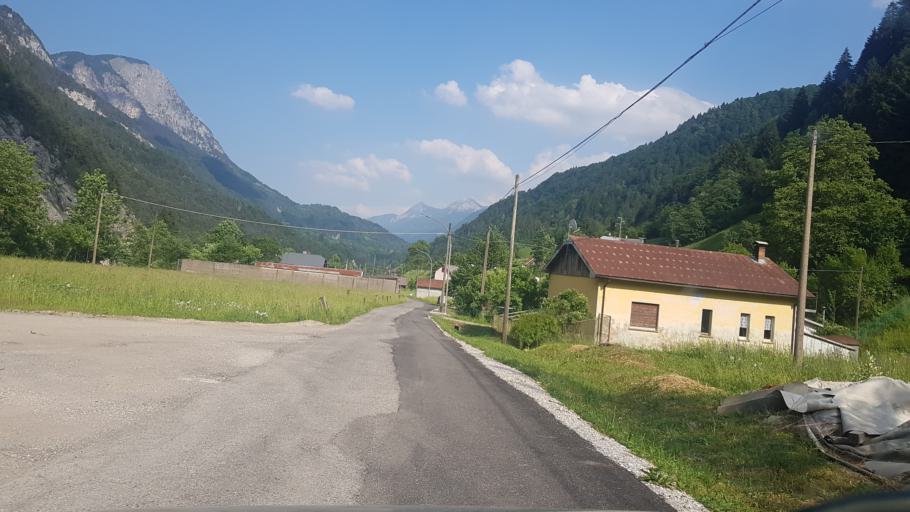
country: IT
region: Friuli Venezia Giulia
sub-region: Provincia di Udine
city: Pontebba
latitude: 46.5223
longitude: 13.2662
